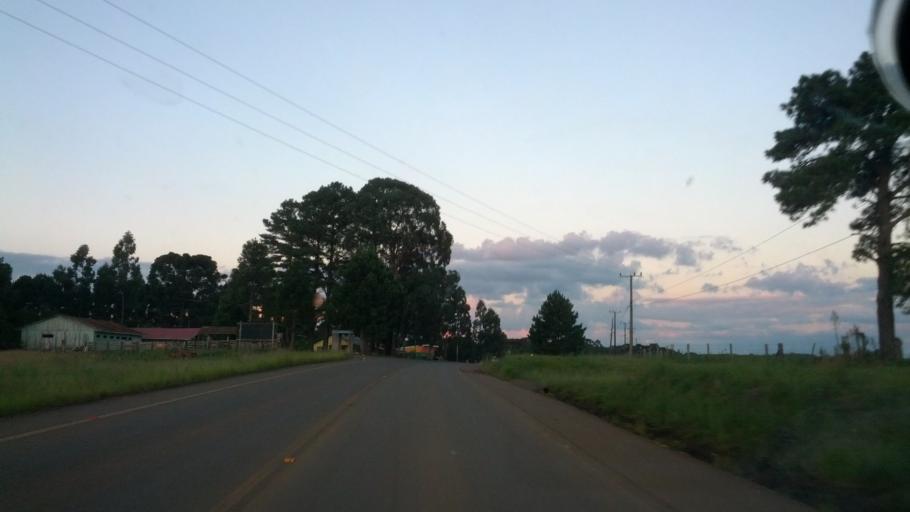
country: BR
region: Rio Grande do Sul
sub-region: Vacaria
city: Estrela
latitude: -27.8972
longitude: -50.7751
